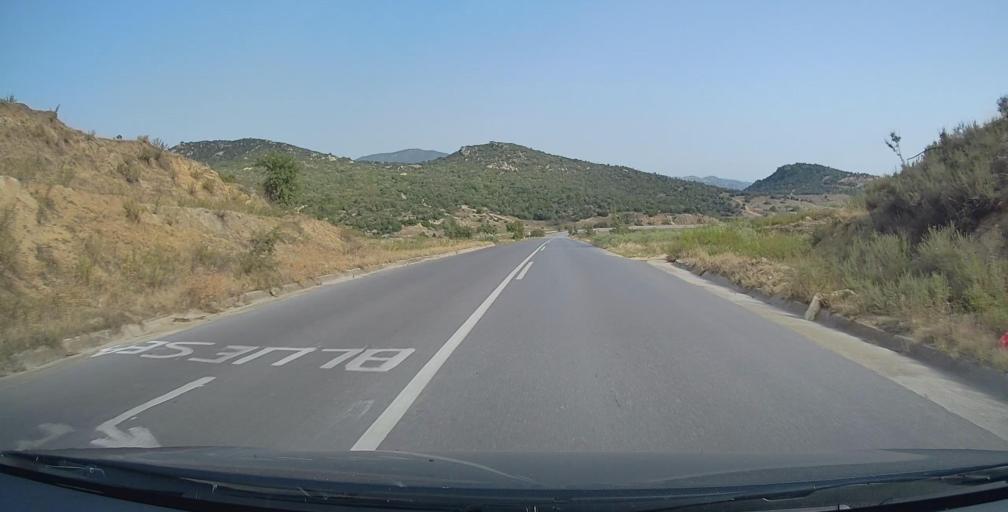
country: GR
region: Central Macedonia
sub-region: Nomos Chalkidikis
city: Sykia
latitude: 40.0192
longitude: 23.9865
